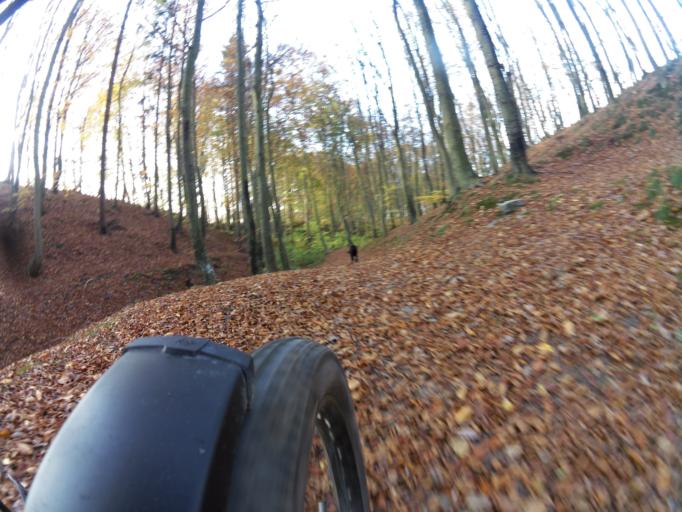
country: PL
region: Pomeranian Voivodeship
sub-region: Powiat pucki
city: Krokowa
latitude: 54.7704
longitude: 18.1750
